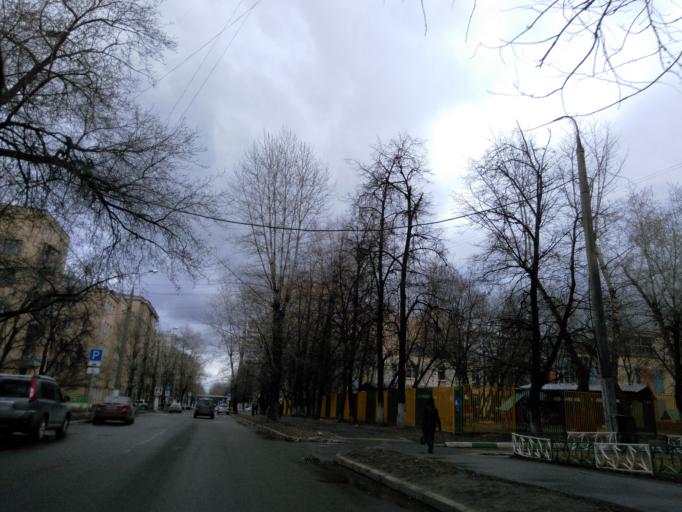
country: RU
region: Moscow
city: Zamoskvorech'ye
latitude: 55.7147
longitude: 37.6106
